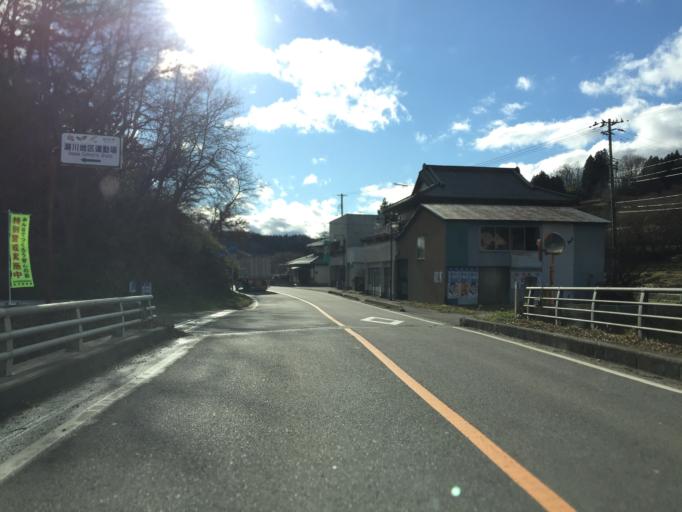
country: JP
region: Fukushima
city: Funehikimachi-funehiki
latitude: 37.4913
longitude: 140.5758
